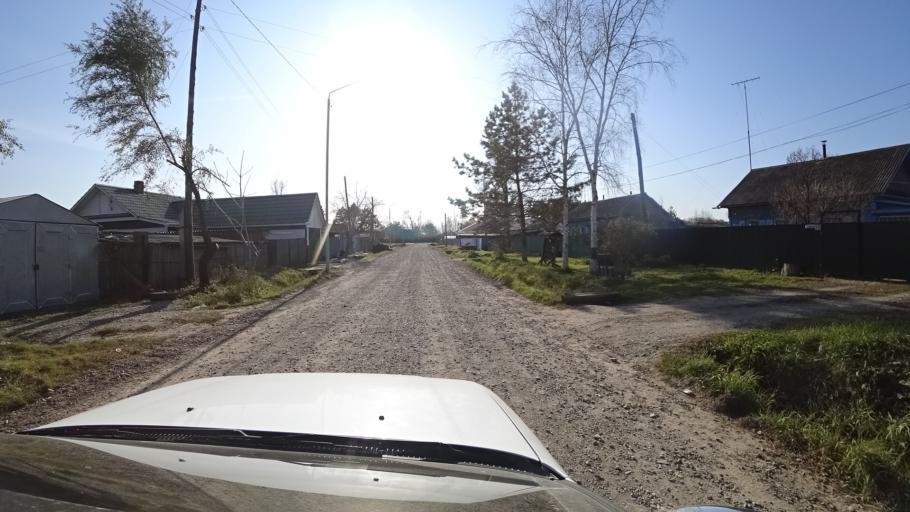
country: RU
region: Primorskiy
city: Dal'nerechensk
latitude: 45.9235
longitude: 133.7487
